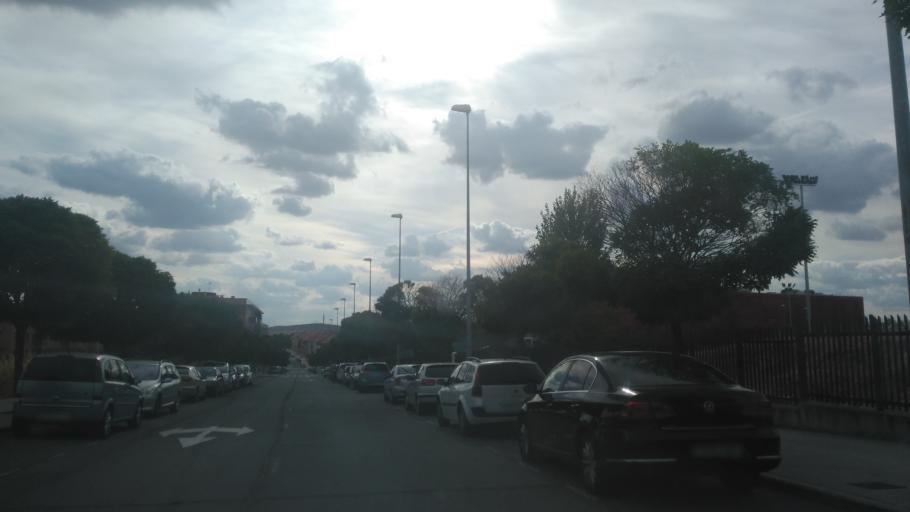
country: ES
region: Castille and Leon
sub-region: Provincia de Salamanca
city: Salamanca
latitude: 40.9704
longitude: -5.6810
